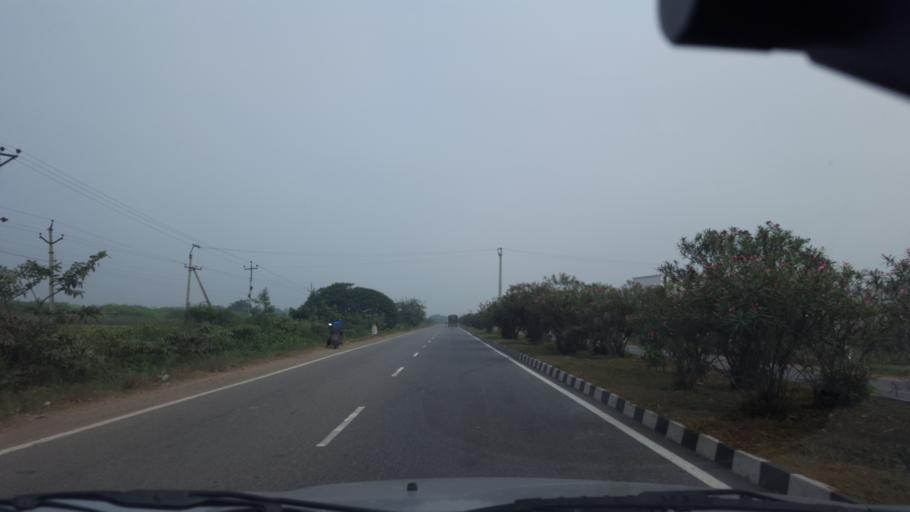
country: IN
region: Andhra Pradesh
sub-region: Guntur
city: Chilakalurupet
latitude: 16.0660
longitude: 80.1513
